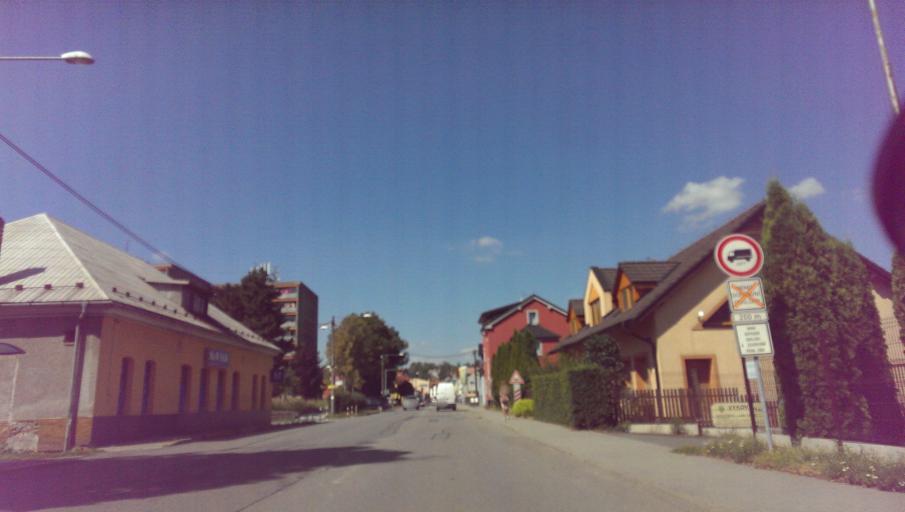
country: CZ
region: Moravskoslezsky
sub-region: Okres Novy Jicin
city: Pribor
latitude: 49.6422
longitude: 18.1518
